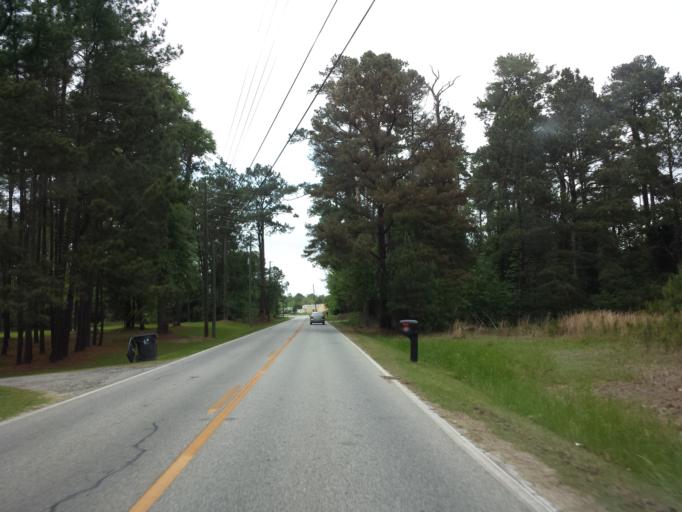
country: US
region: Georgia
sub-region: Lowndes County
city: Hahira
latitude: 31.0038
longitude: -83.3752
